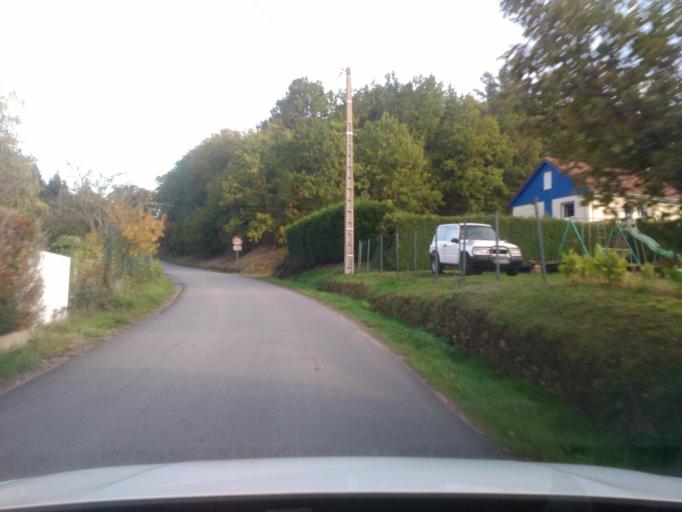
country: FR
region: Lorraine
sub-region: Departement des Vosges
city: Taintrux
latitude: 48.2478
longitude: 6.9075
